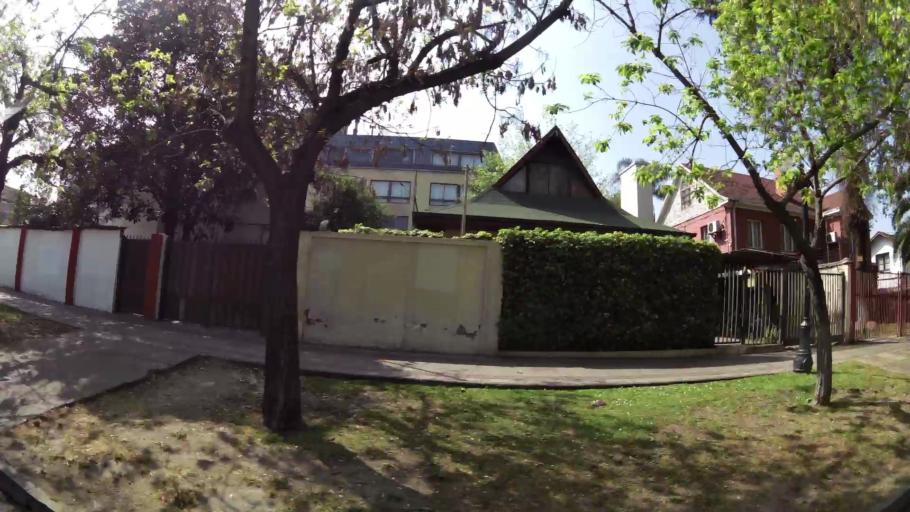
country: CL
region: Santiago Metropolitan
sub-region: Provincia de Santiago
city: Villa Presidente Frei, Nunoa, Santiago, Chile
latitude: -33.4399
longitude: -70.6018
